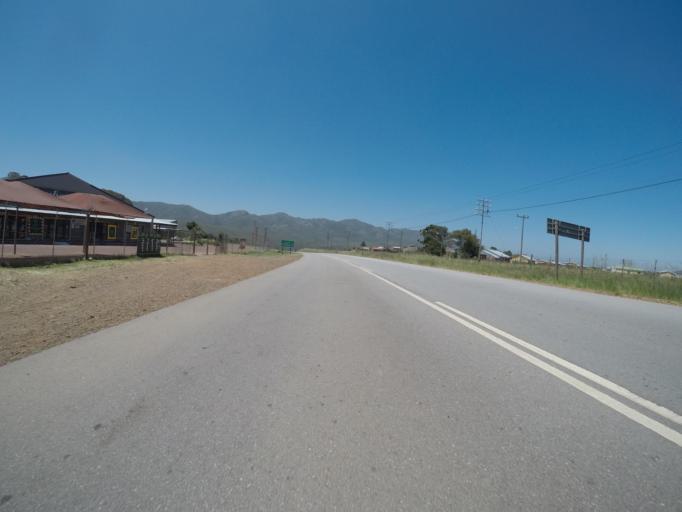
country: ZA
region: Eastern Cape
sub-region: Cacadu District Municipality
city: Kareedouw
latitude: -33.9519
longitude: 24.2997
